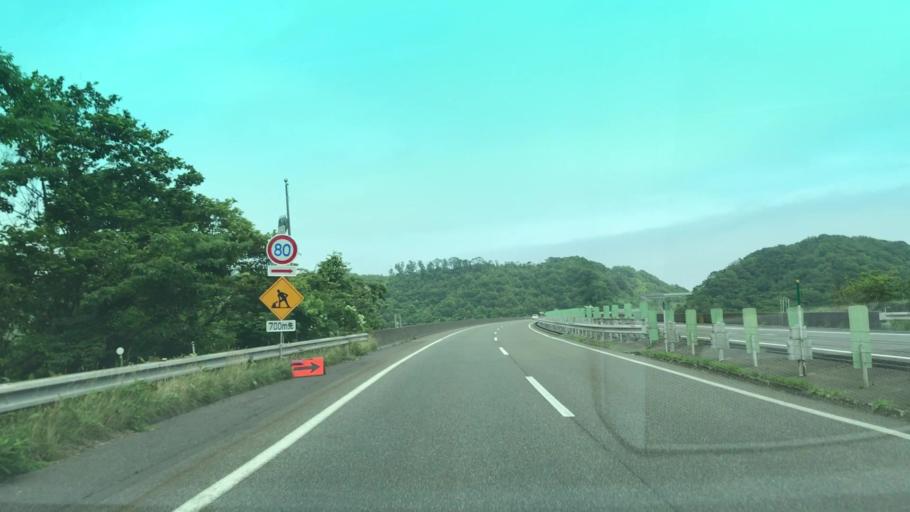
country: JP
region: Hokkaido
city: Shiraoi
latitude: 42.4938
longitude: 141.2423
